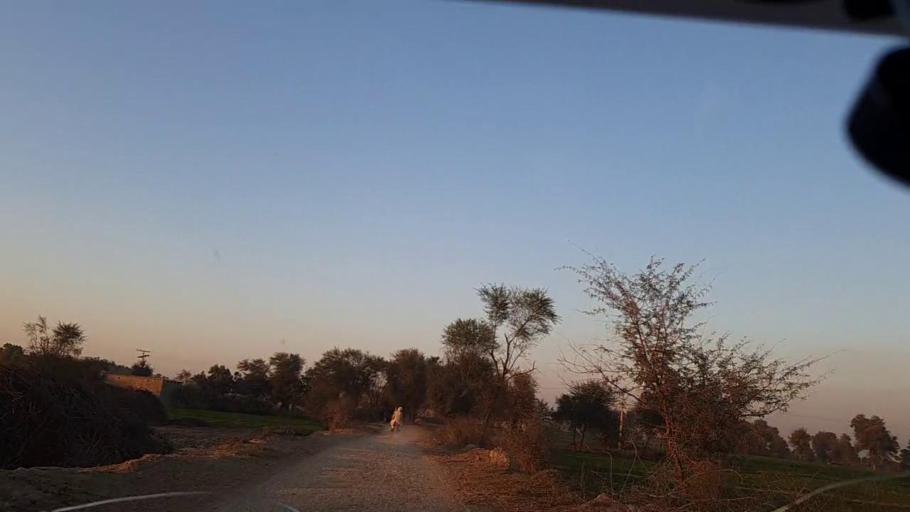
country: PK
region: Sindh
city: Adilpur
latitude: 27.8402
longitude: 69.2982
